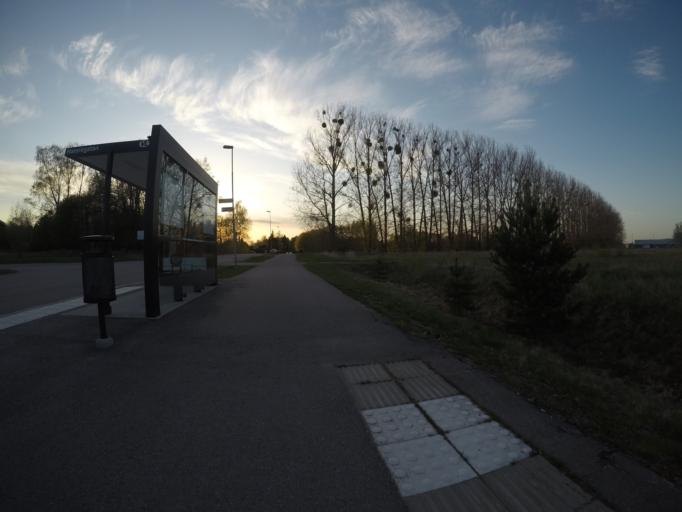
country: SE
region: Vaestmanland
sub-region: Vasteras
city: Vasteras
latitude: 59.5933
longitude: 16.6131
